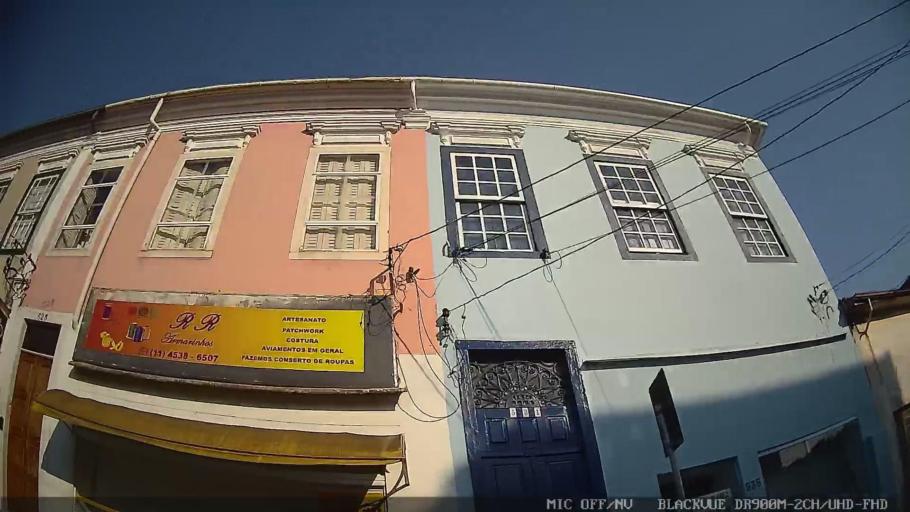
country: BR
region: Sao Paulo
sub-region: Itatiba
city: Itatiba
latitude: -23.0069
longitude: -46.8435
